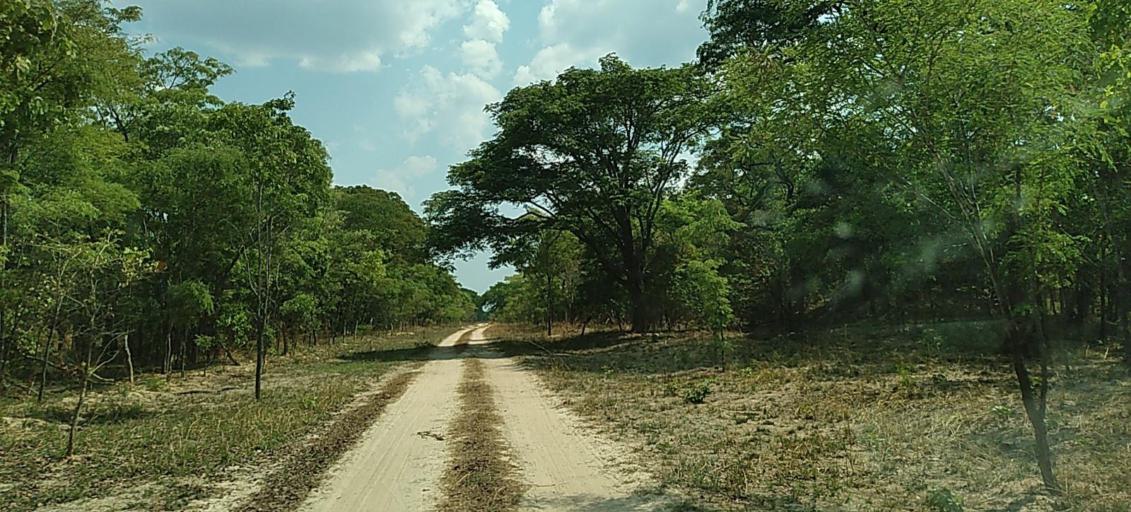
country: ZM
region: Copperbelt
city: Mpongwe
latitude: -13.8463
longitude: 27.9334
